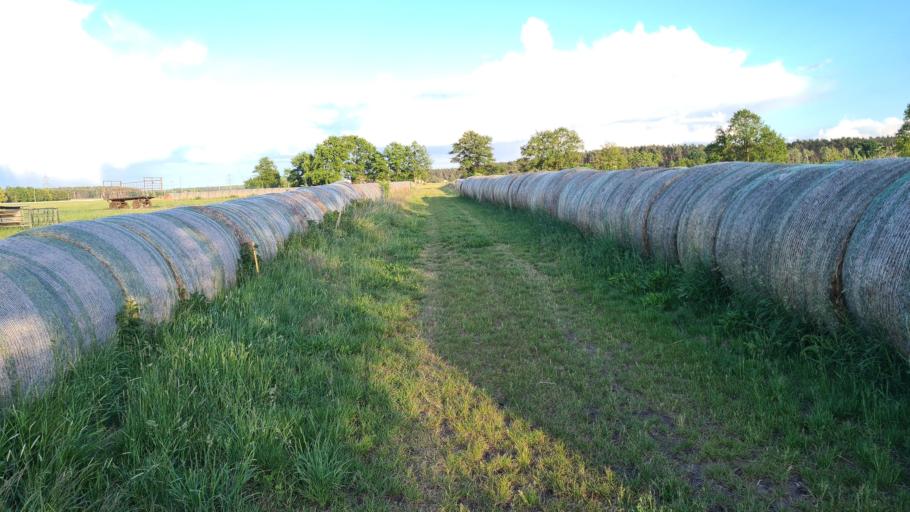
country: DE
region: Brandenburg
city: Schilda
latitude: 51.6143
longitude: 13.3511
